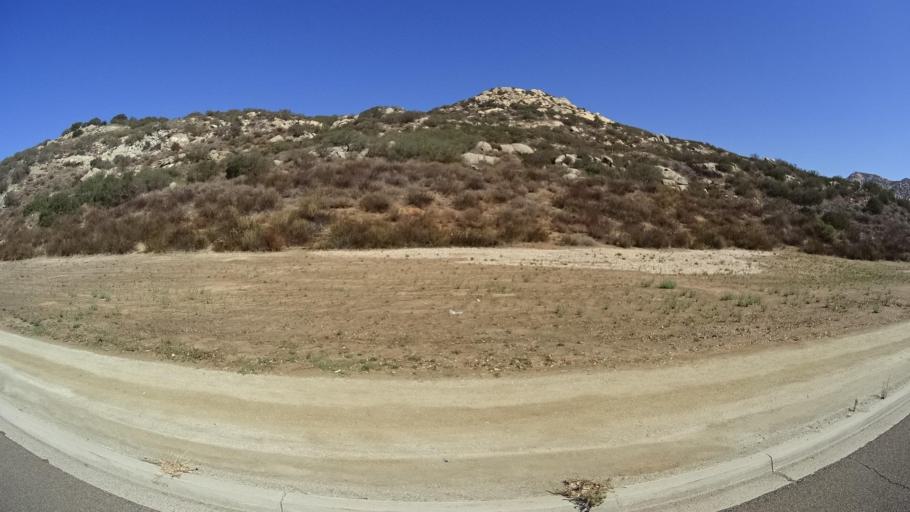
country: US
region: California
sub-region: San Diego County
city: San Diego Country Estates
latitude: 33.0028
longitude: -116.8046
